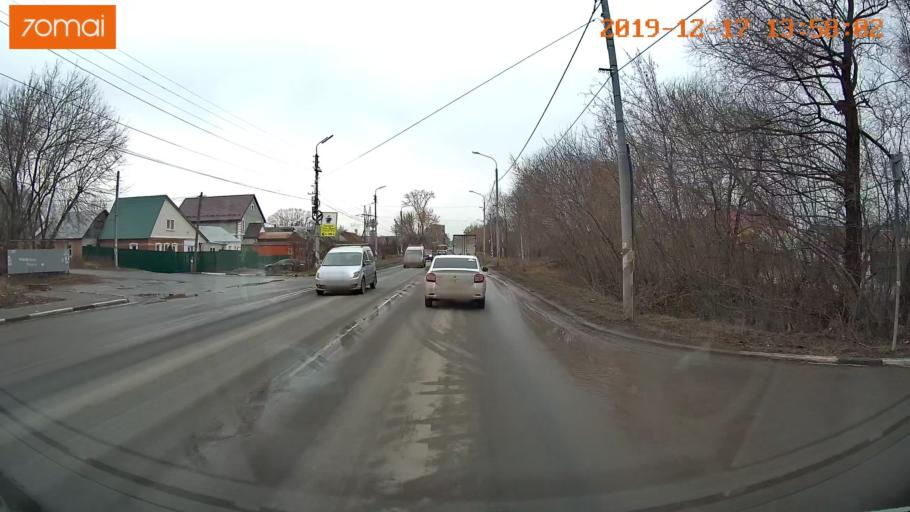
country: RU
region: Rjazan
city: Ryazan'
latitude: 54.6245
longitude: 39.6874
